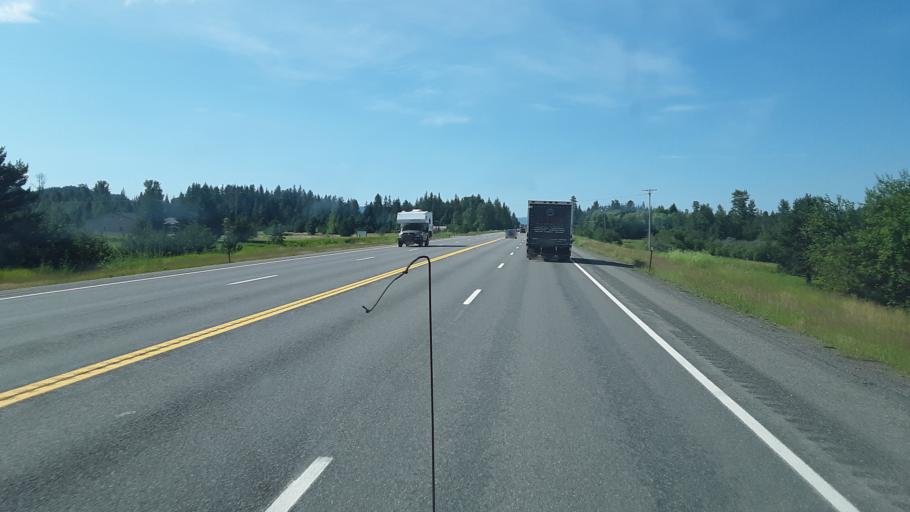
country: US
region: Idaho
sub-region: Bonner County
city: Ponderay
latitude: 48.3516
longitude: -116.5476
